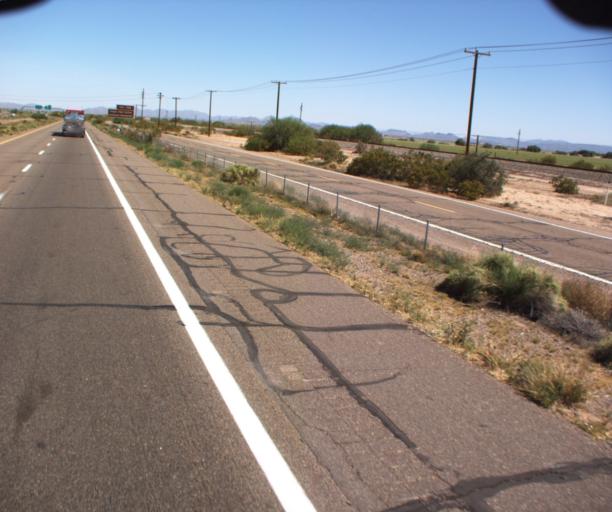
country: US
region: Arizona
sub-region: Maricopa County
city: Gila Bend
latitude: 32.9386
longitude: -112.7619
